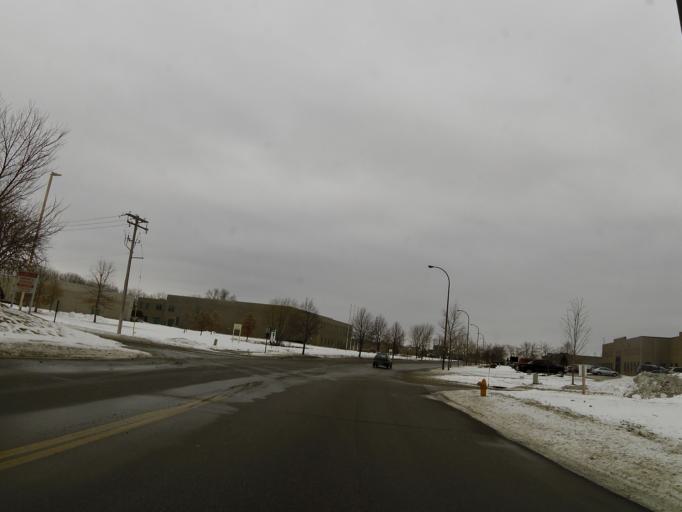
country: US
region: Minnesota
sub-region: Dakota County
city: South Saint Paul
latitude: 44.8922
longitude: -93.0271
